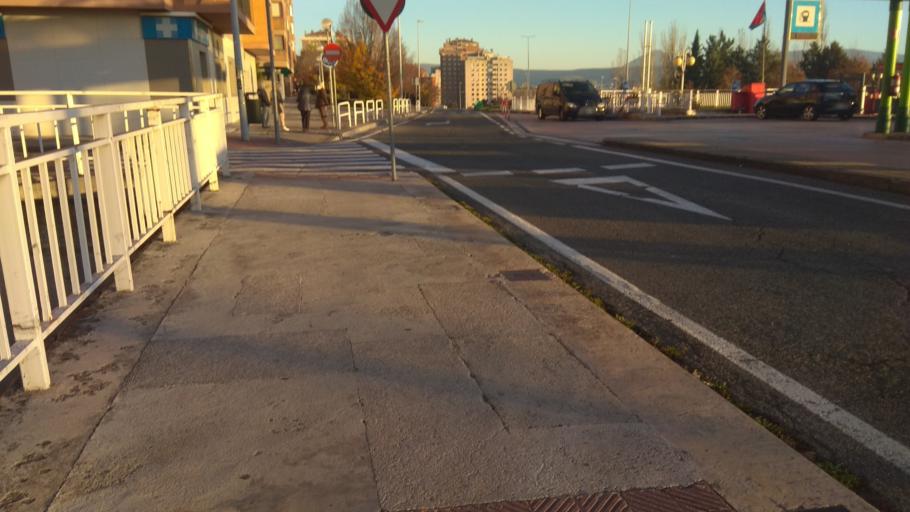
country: ES
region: Navarre
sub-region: Provincia de Navarra
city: Iturrama
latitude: 42.8030
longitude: -1.6520
